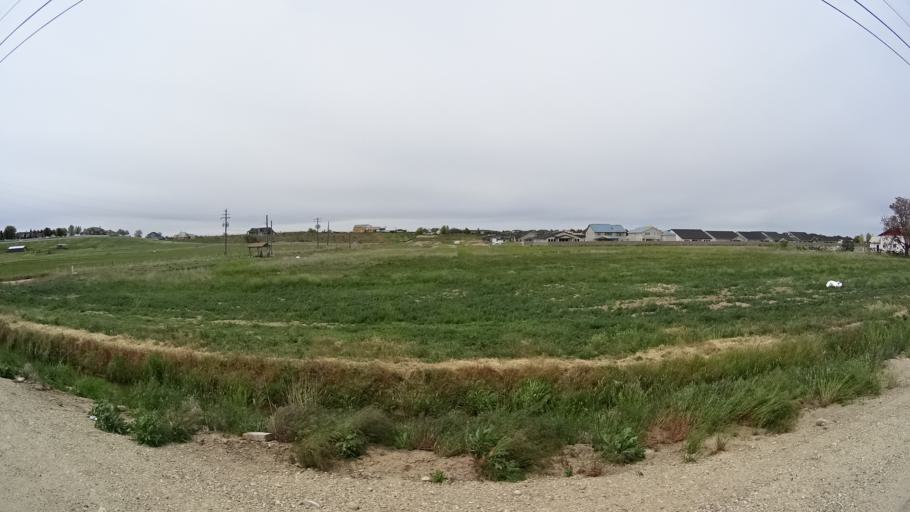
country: US
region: Idaho
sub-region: Ada County
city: Meridian
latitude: 43.5505
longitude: -116.3541
